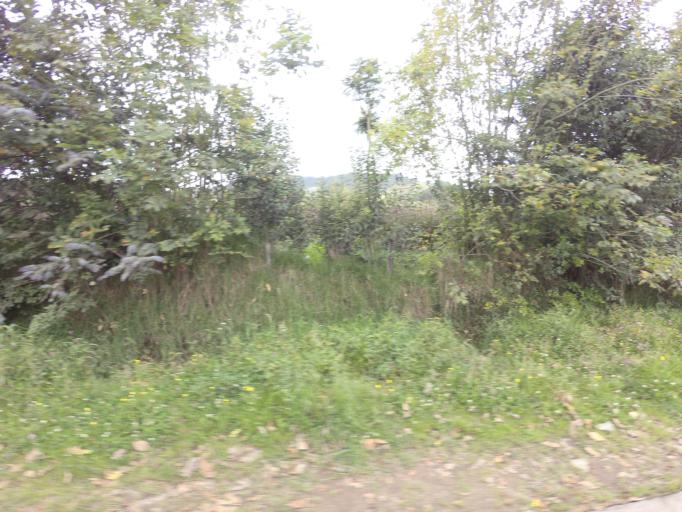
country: CO
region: Cundinamarca
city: Tabio
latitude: 4.9624
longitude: -74.0692
